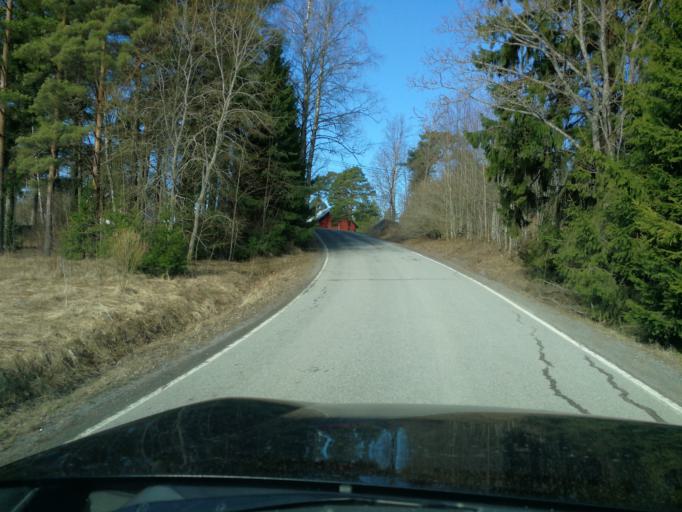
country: FI
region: Uusimaa
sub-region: Raaseporin
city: Inga
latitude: 60.0509
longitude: 24.0518
